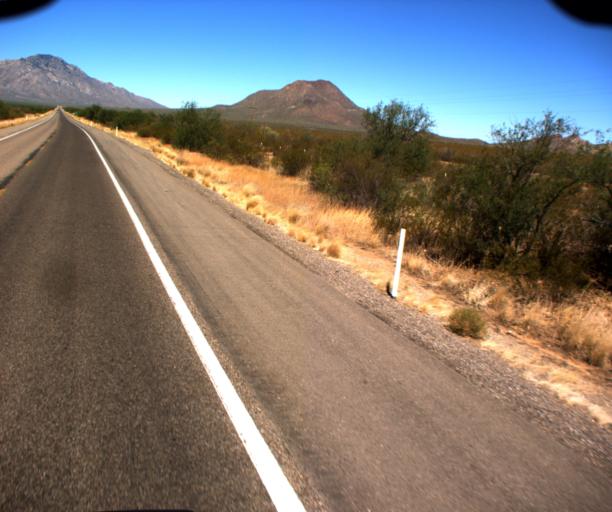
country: US
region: Arizona
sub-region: Pima County
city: Three Points
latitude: 32.0602
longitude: -111.3955
